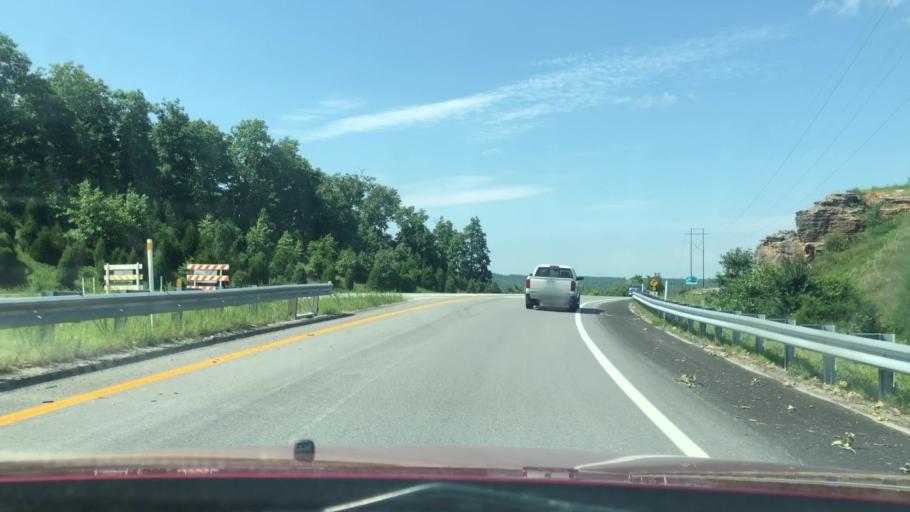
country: US
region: Missouri
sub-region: Taney County
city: Branson
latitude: 36.6785
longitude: -93.3162
